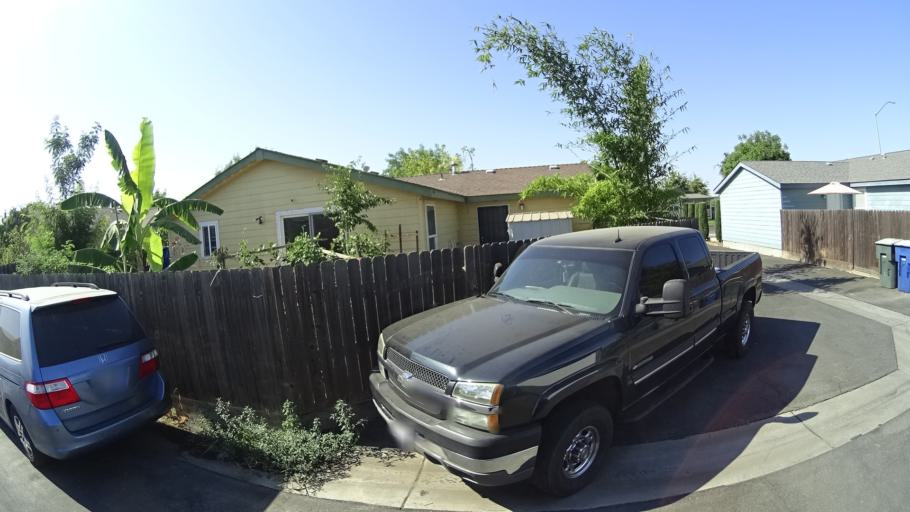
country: US
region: California
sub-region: Fresno County
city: West Park
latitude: 36.7208
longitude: -119.8262
